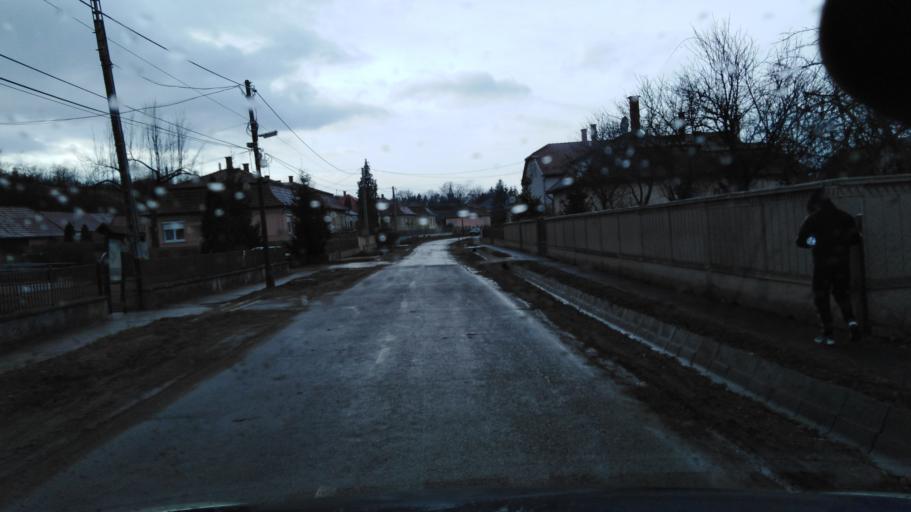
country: HU
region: Nograd
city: Karancskeszi
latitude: 48.1800
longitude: 19.6441
